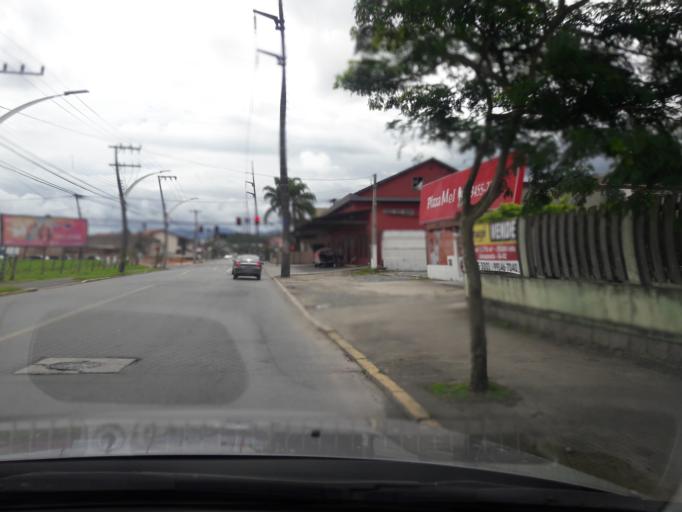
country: BR
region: Santa Catarina
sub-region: Joinville
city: Joinville
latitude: -26.3242
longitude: -48.8577
